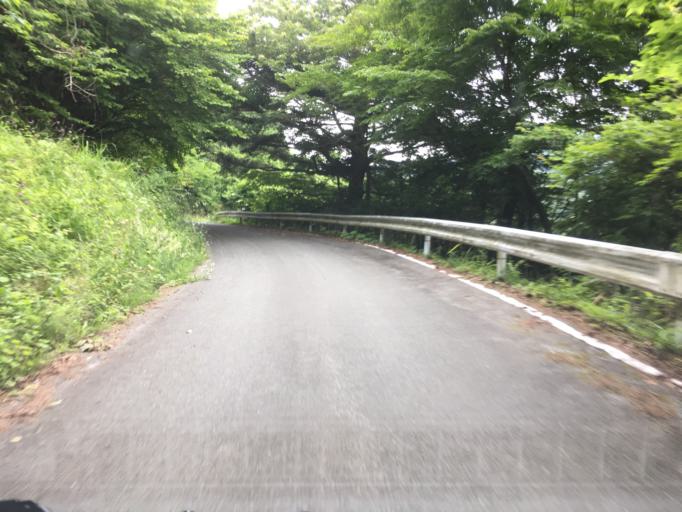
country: JP
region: Miyagi
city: Marumori
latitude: 37.7738
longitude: 140.8317
